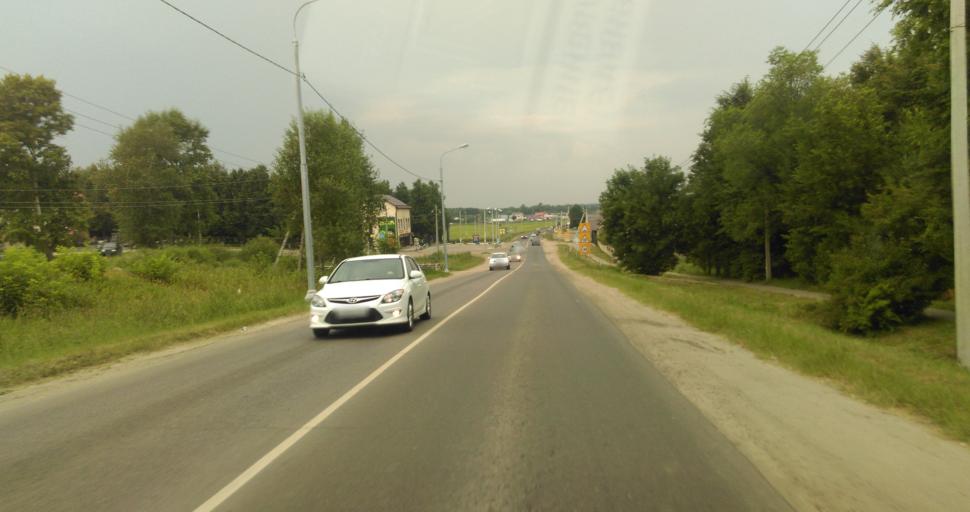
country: RU
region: Moskovskaya
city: Zhitnevo
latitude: 55.3440
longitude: 37.9036
